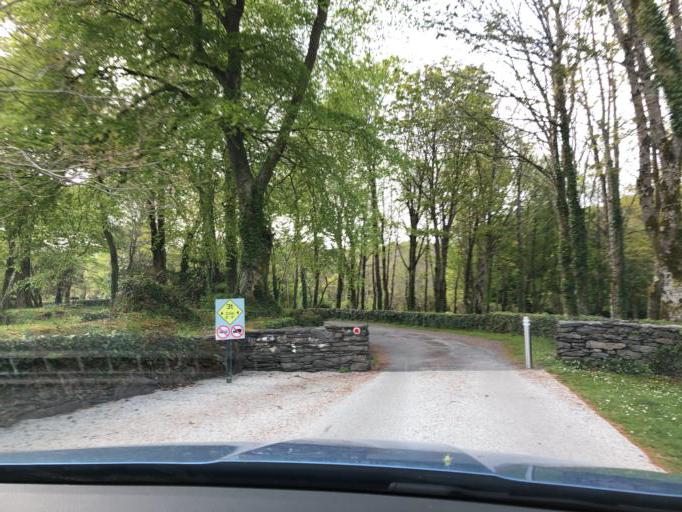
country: IE
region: Munster
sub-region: Ciarrai
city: Cahersiveen
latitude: 51.7631
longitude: -10.1289
